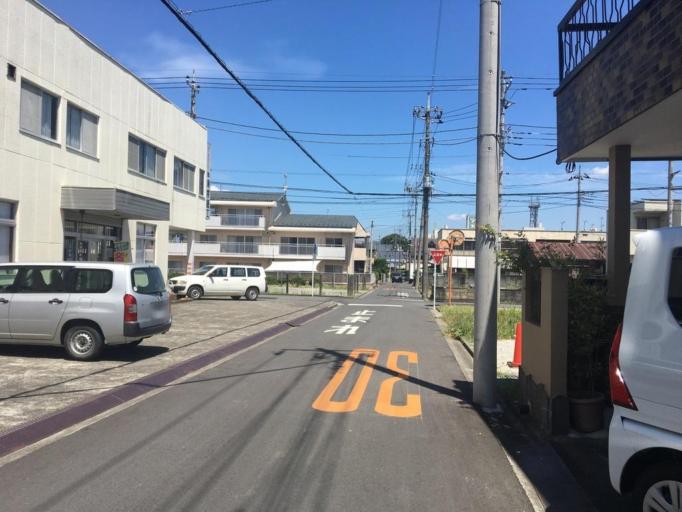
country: JP
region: Saitama
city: Chichibu
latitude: 35.9899
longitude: 139.0776
